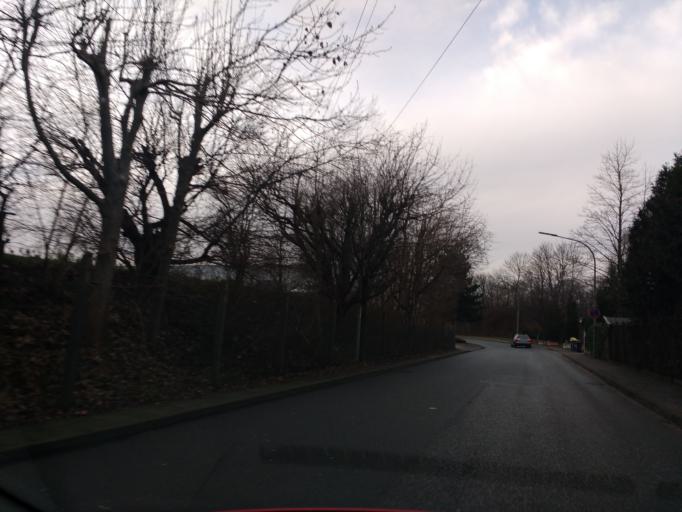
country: DE
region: North Rhine-Westphalia
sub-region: Regierungsbezirk Detmold
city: Paderborn
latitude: 51.7009
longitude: 8.7331
